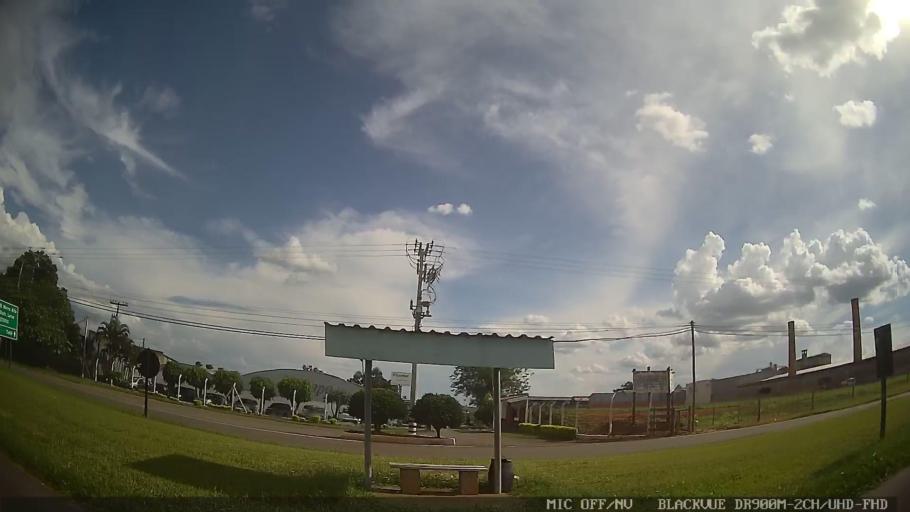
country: BR
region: Sao Paulo
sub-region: Laranjal Paulista
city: Laranjal Paulista
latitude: -23.0386
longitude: -47.8540
